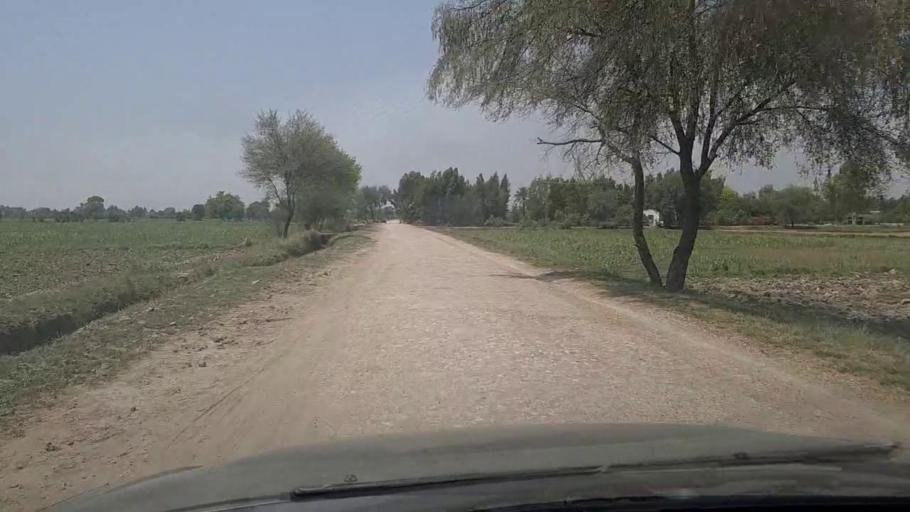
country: PK
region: Sindh
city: Adilpur
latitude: 27.9307
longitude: 69.2496
